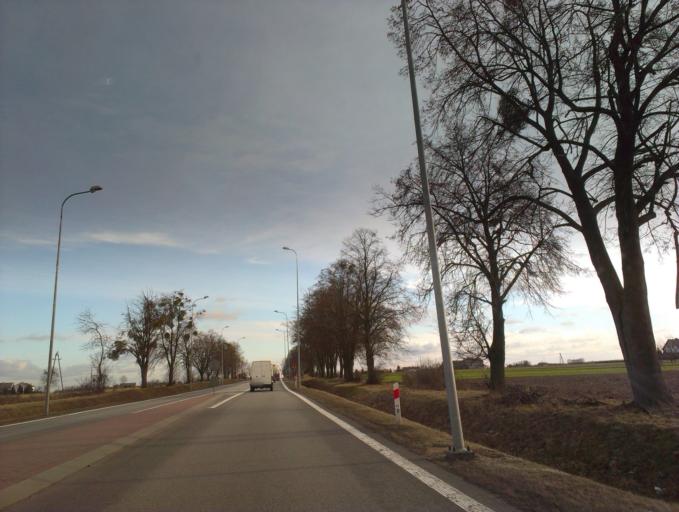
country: PL
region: Kujawsko-Pomorskie
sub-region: Powiat lipnowski
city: Kikol
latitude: 52.9334
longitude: 19.0622
